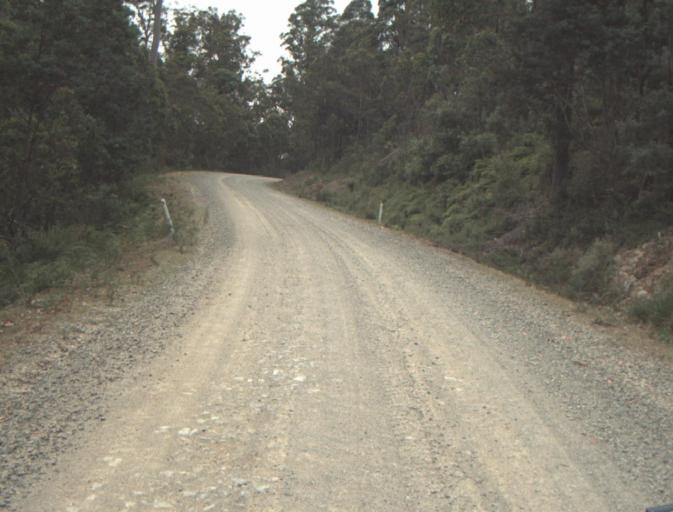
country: AU
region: Tasmania
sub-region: Dorset
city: Scottsdale
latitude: -41.3892
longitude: 147.5074
